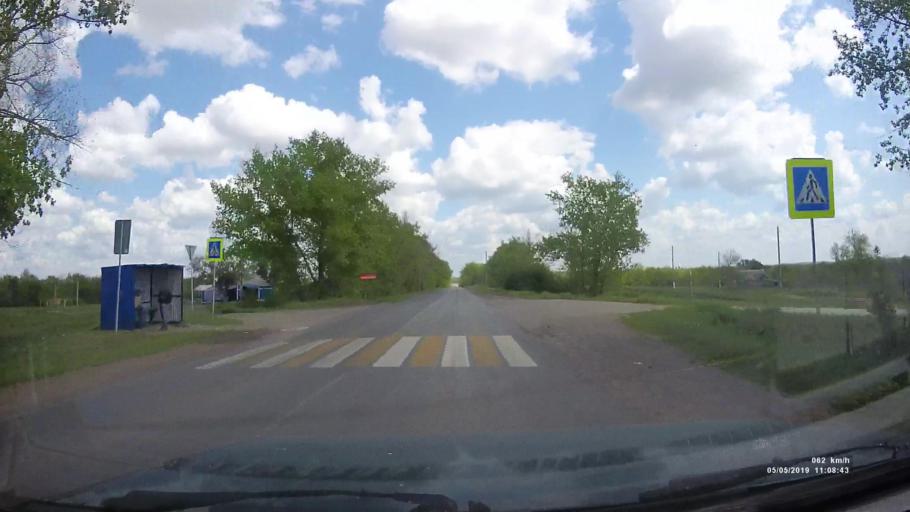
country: RU
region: Rostov
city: Ust'-Donetskiy
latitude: 47.7360
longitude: 40.9172
